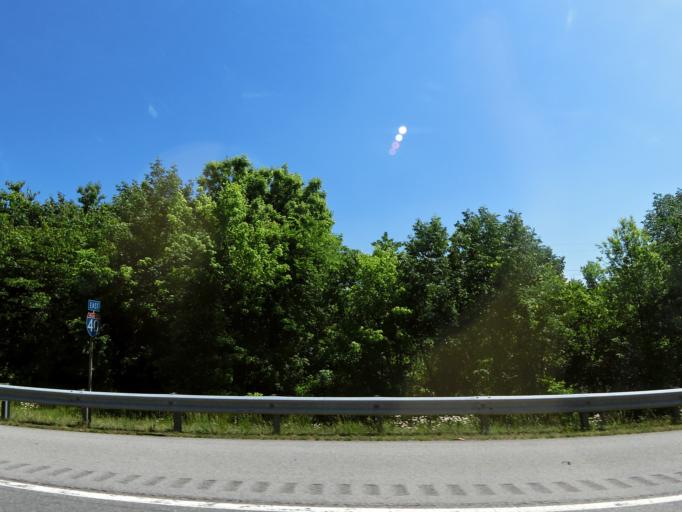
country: US
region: Tennessee
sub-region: Knox County
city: Mascot
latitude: 35.9963
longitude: -83.6914
